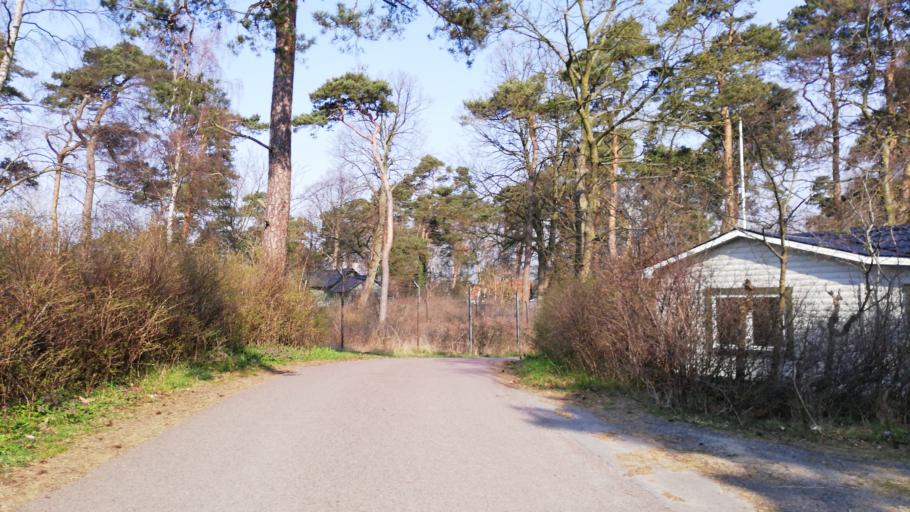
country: SE
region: Skane
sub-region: Ystads Kommun
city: Ystad
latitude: 55.4275
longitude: 13.8426
